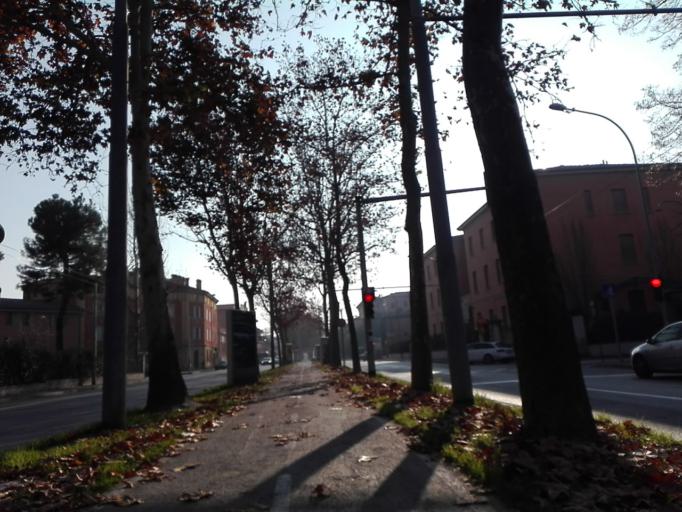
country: IT
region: Emilia-Romagna
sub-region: Provincia di Bologna
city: Bologna
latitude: 44.4952
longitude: 11.3569
